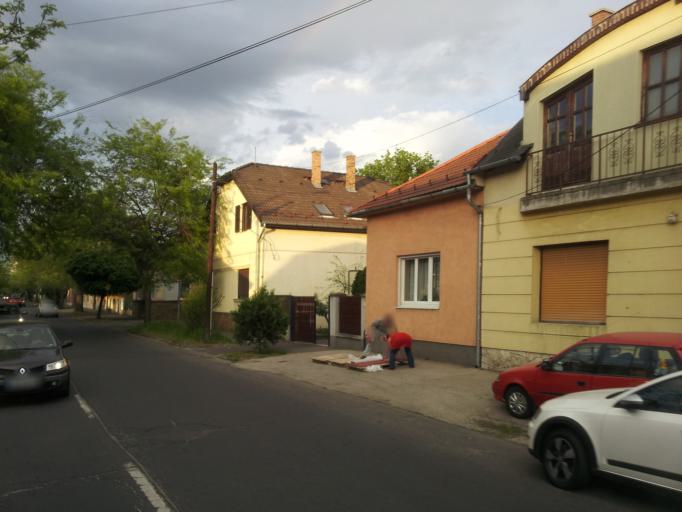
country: HU
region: Budapest
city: Budapest XV. keruelet
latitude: 47.5435
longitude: 19.1094
